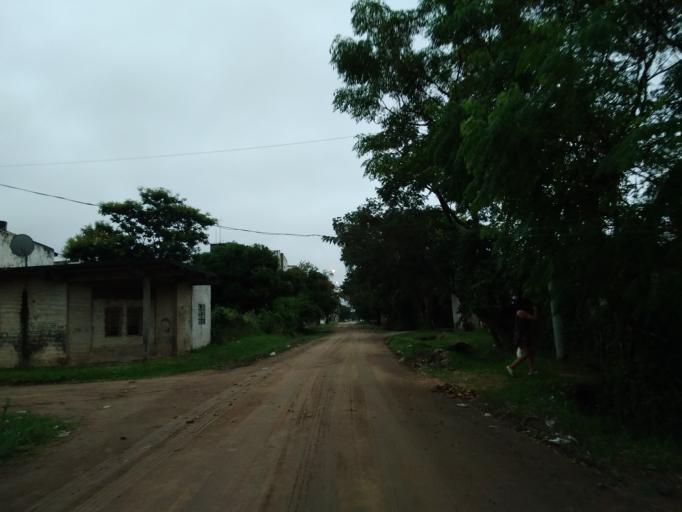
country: AR
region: Corrientes
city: Corrientes
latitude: -27.4874
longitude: -58.8211
